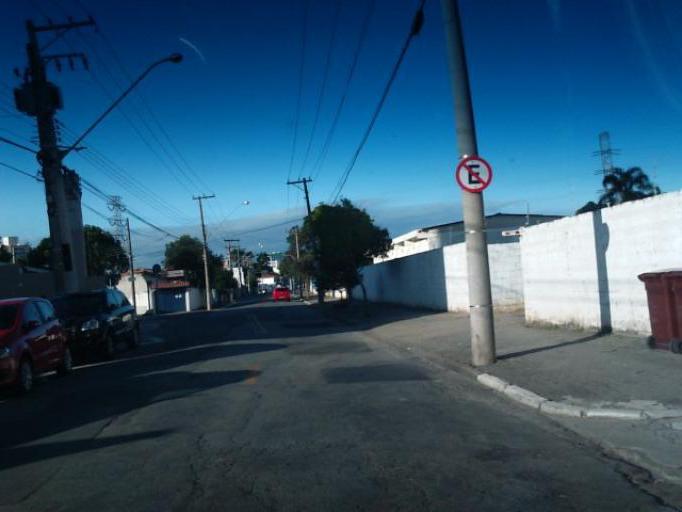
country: BR
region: Sao Paulo
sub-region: Sao Jose Dos Campos
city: Sao Jose dos Campos
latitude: -23.1948
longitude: -45.8807
